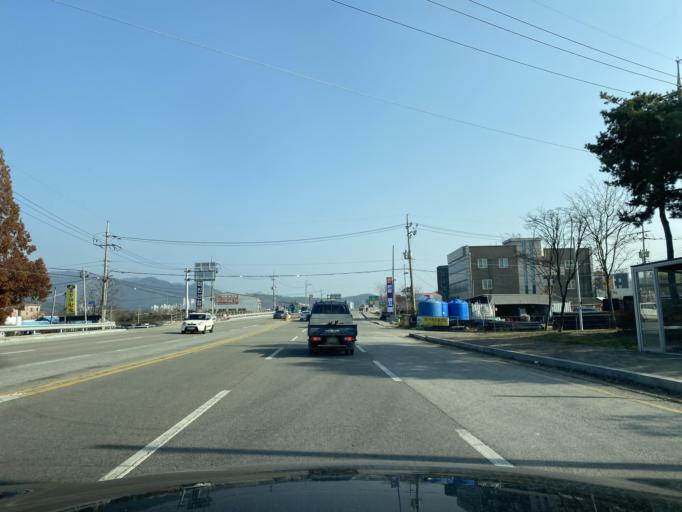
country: KR
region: Chungcheongnam-do
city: Yesan
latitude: 36.6849
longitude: 126.8162
